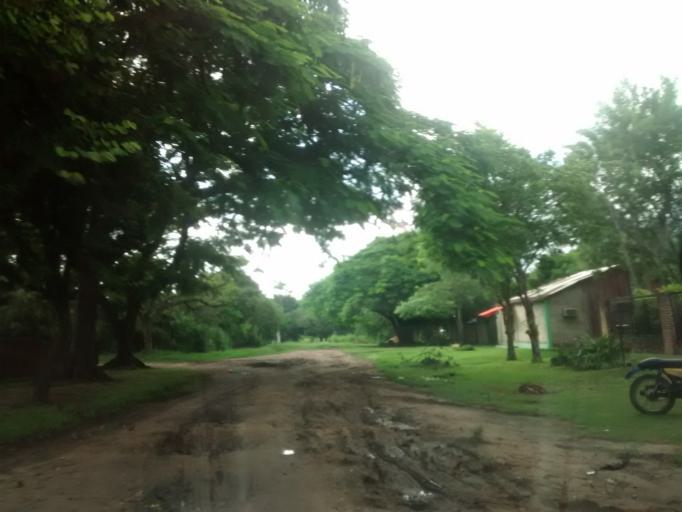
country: AR
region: Chaco
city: Puerto Tirol
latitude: -27.3773
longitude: -59.0886
